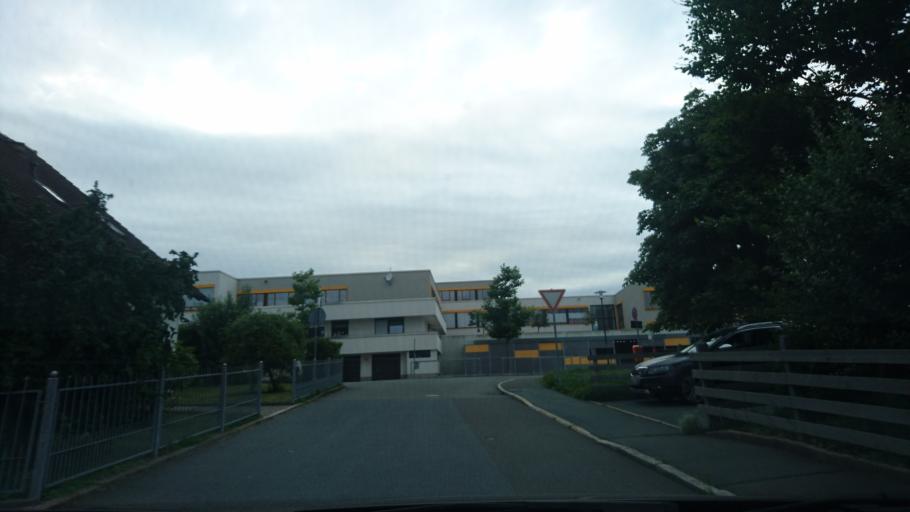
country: DE
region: Bavaria
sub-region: Upper Franconia
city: Naila
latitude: 50.3355
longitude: 11.7019
